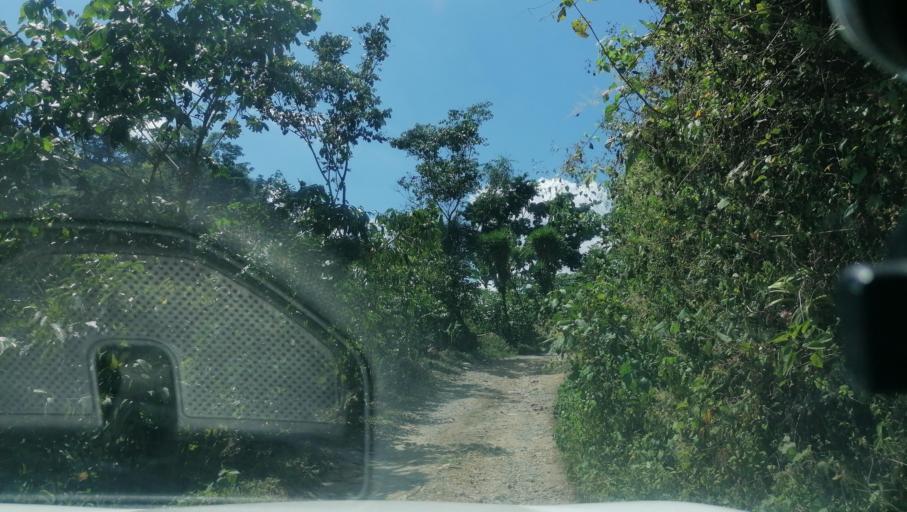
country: MX
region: Chiapas
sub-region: Union Juarez
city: Santo Domingo
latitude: 15.0702
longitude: -92.1342
